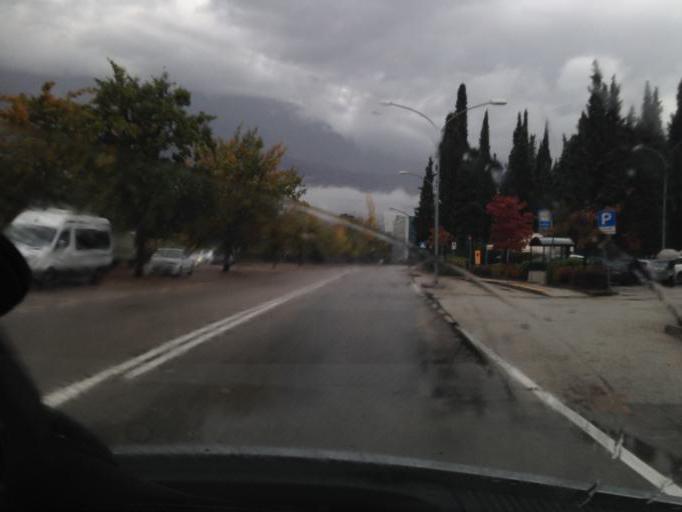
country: IT
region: Trentino-Alto Adige
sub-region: Provincia di Trento
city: Rovereto
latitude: 45.8961
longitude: 11.0372
